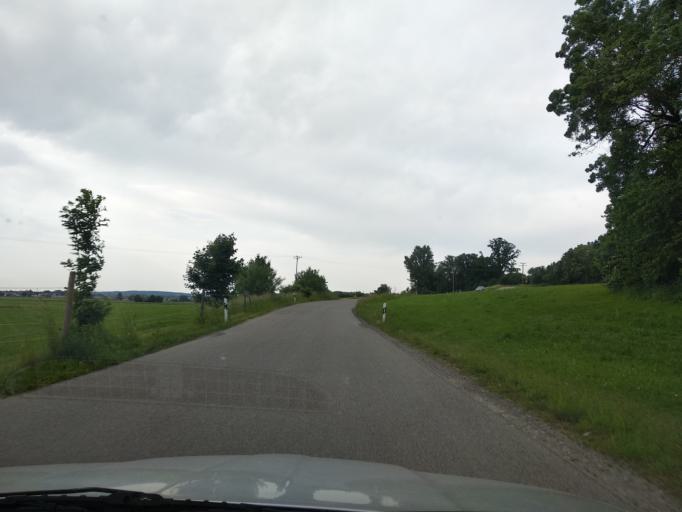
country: DE
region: Bavaria
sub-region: Swabia
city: Lachen
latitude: 47.9493
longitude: 10.2218
